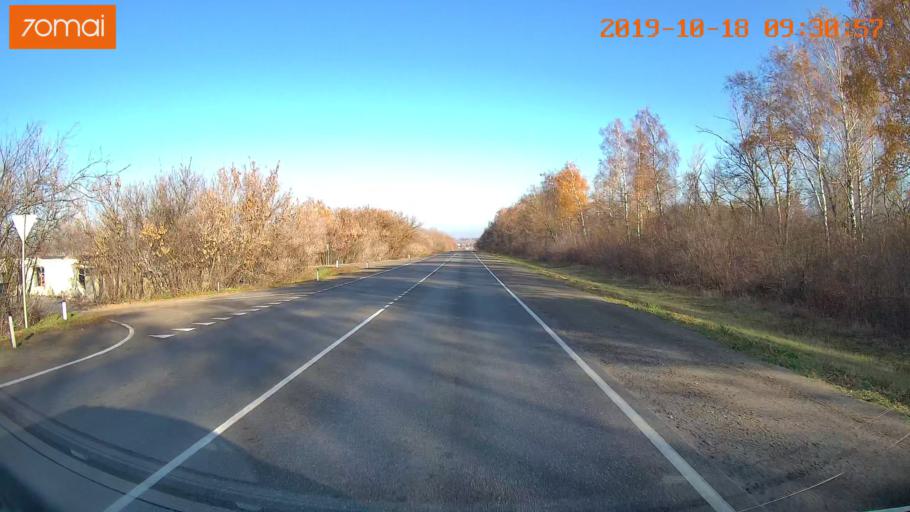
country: RU
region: Tula
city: Yefremov
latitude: 53.1445
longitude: 38.1588
